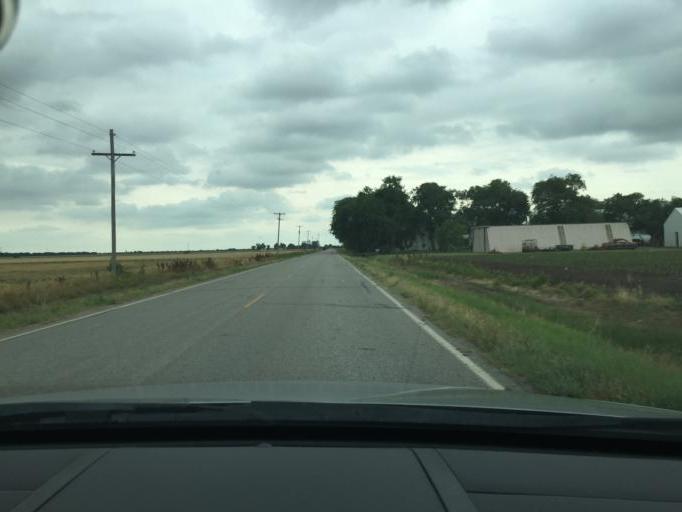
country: US
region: Kansas
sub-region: Reno County
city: South Hutchinson
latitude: 37.9796
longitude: -98.0138
